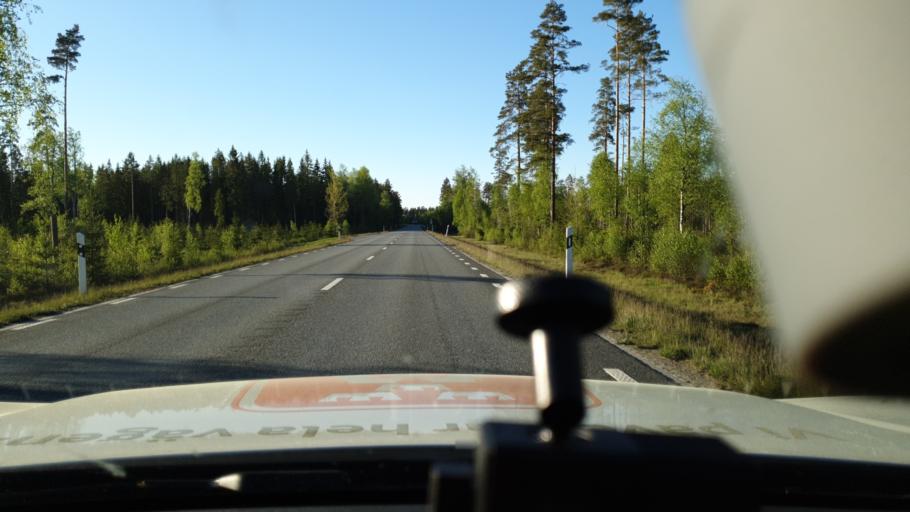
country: SE
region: Joenkoeping
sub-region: Eksjo Kommun
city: Eksjoe
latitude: 57.6280
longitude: 14.9690
